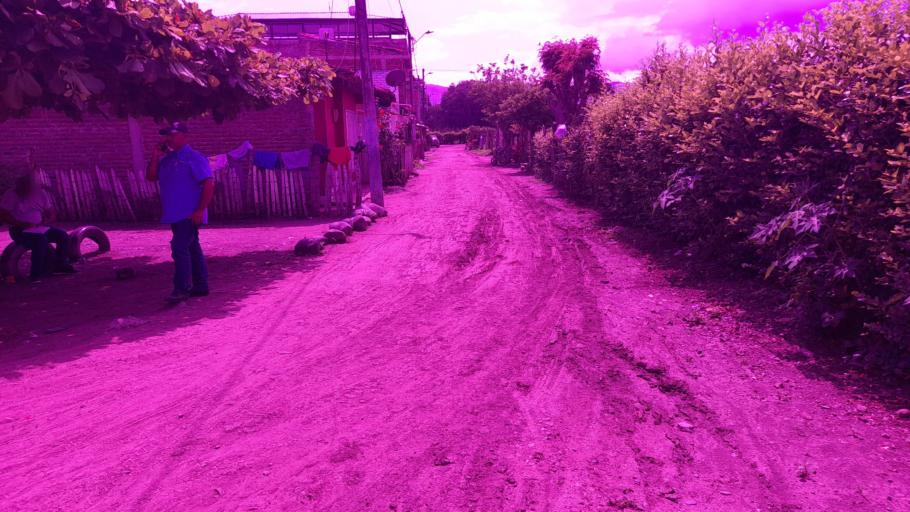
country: CO
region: Valle del Cauca
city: Guacari
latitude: 3.7601
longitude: -76.3616
